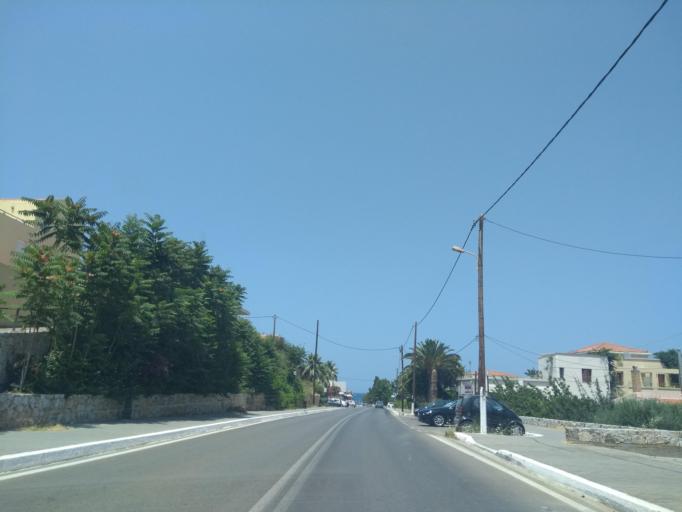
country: GR
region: Crete
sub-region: Nomos Chanias
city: Daratsos
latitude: 35.5085
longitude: 23.9883
